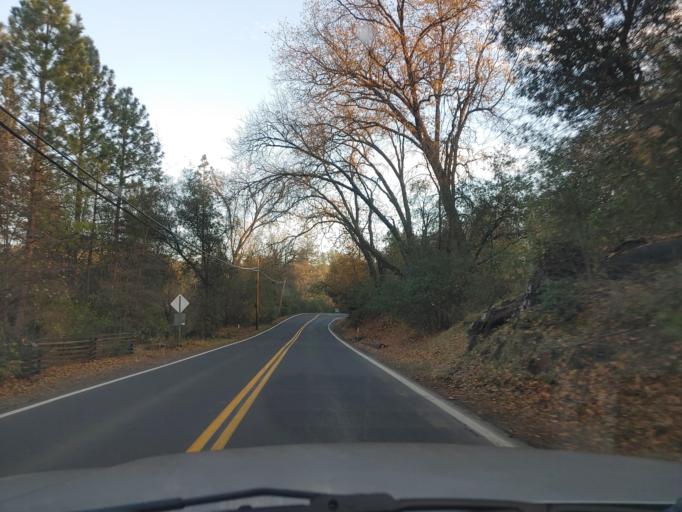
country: US
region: California
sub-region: Tuolumne County
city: Columbia
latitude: 38.0193
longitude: -120.3969
